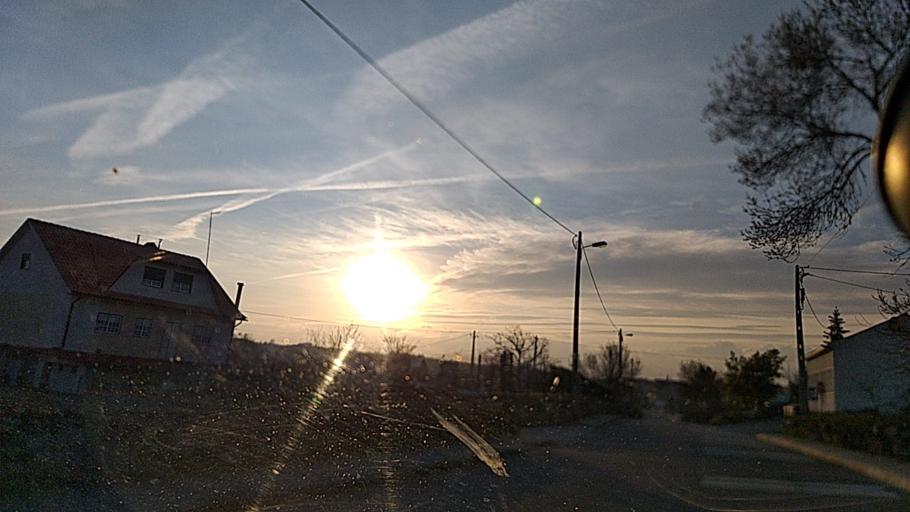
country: PT
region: Guarda
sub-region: Guarda
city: Sequeira
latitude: 40.6015
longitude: -7.0609
